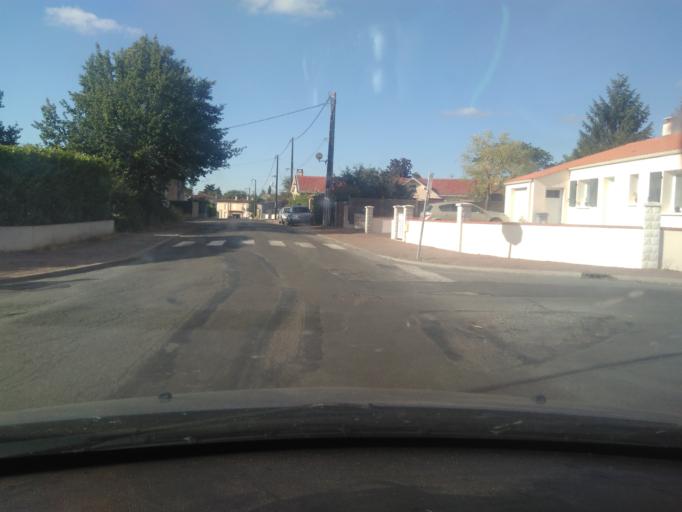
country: FR
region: Pays de la Loire
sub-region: Departement de la Vendee
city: Saint-Florent-des-Bois
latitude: 46.5910
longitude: -1.3147
